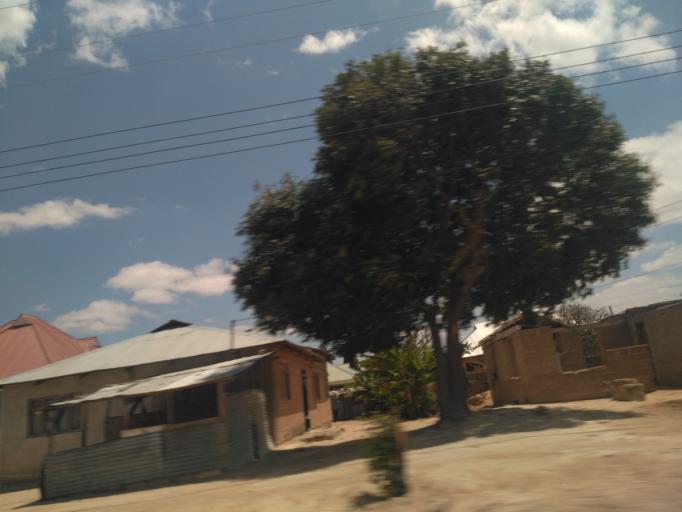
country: TZ
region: Dodoma
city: Kisasa
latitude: -6.1652
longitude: 35.7948
